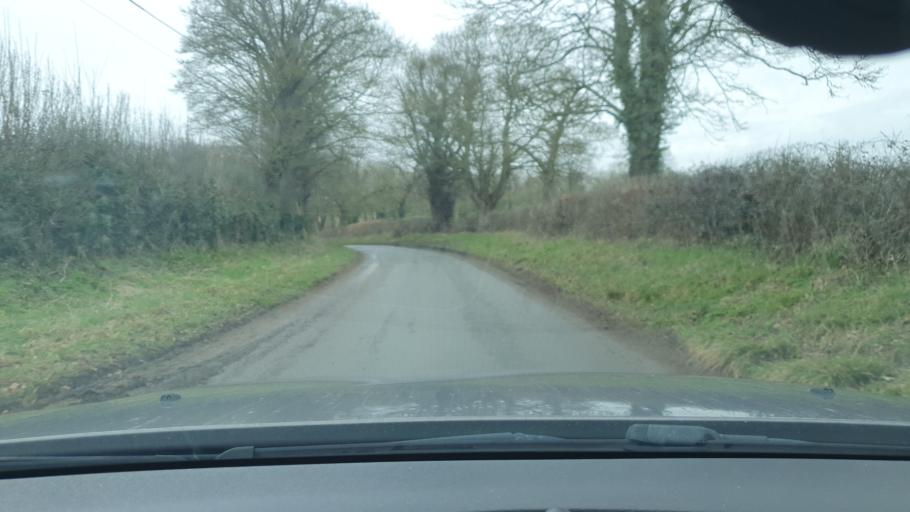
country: GB
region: England
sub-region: West Berkshire
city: Kintbury
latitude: 51.3998
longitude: -1.4661
